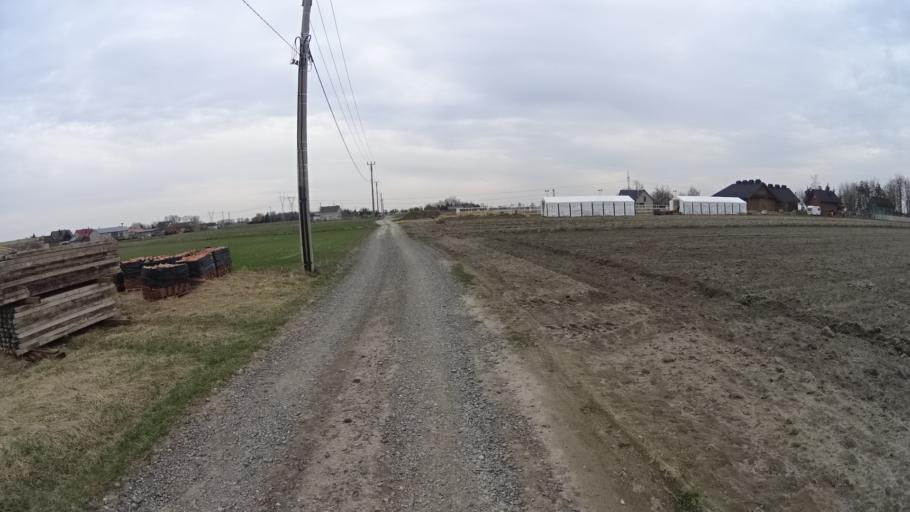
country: PL
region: Masovian Voivodeship
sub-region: Powiat warszawski zachodni
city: Jozefow
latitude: 52.2435
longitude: 20.6885
